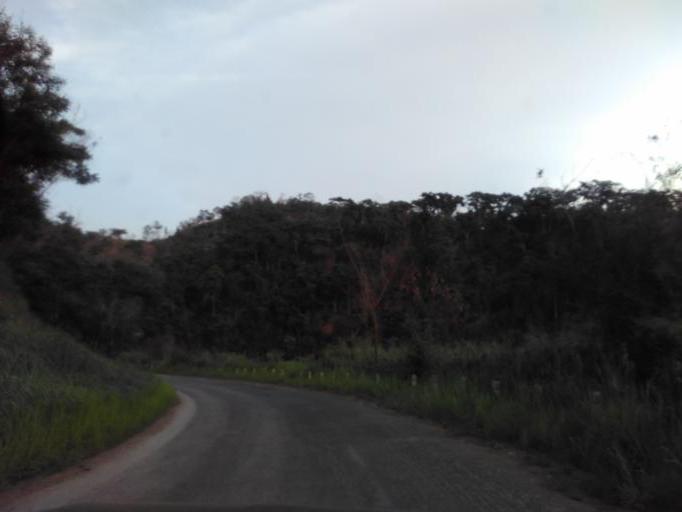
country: GH
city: Bekwai
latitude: 6.5513
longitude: -1.4271
